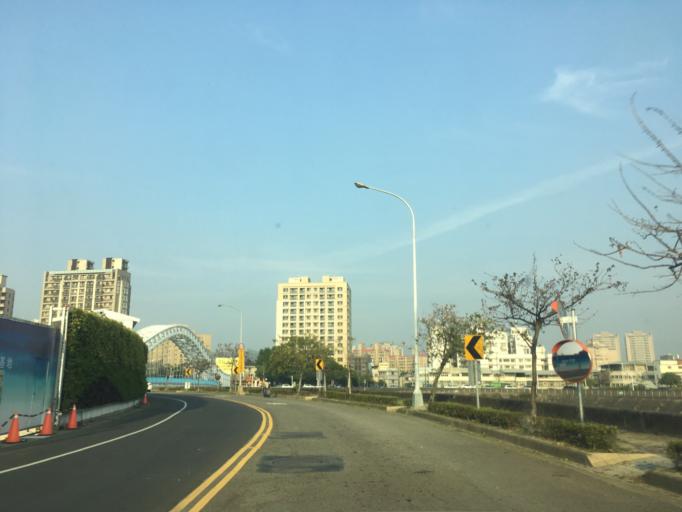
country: TW
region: Taiwan
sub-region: Taichung City
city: Taichung
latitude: 24.1737
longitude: 120.7088
